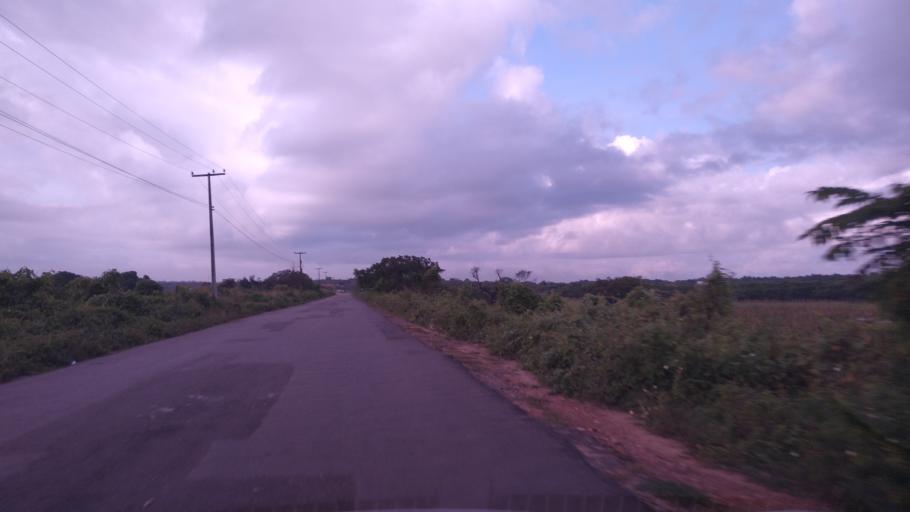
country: BR
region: Ceara
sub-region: Chorozinho
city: Chorozinho
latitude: -4.3075
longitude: -38.4982
